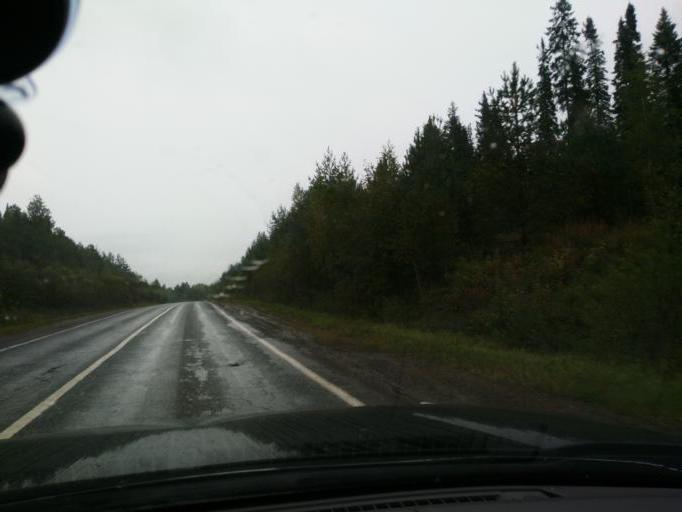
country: RU
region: Perm
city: Yugo-Kamskiy
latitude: 57.6563
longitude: 55.5970
